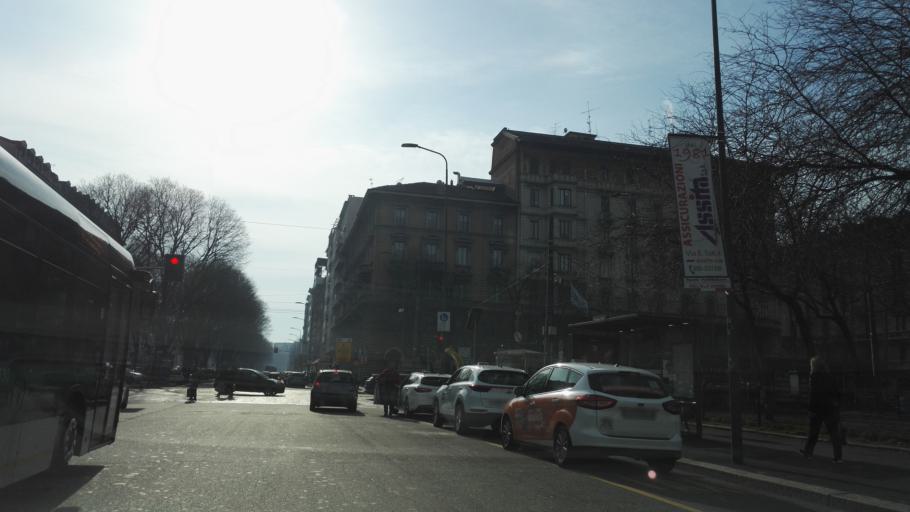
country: IT
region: Lombardy
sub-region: Citta metropolitana di Milano
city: Milano
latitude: 45.4665
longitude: 9.1659
